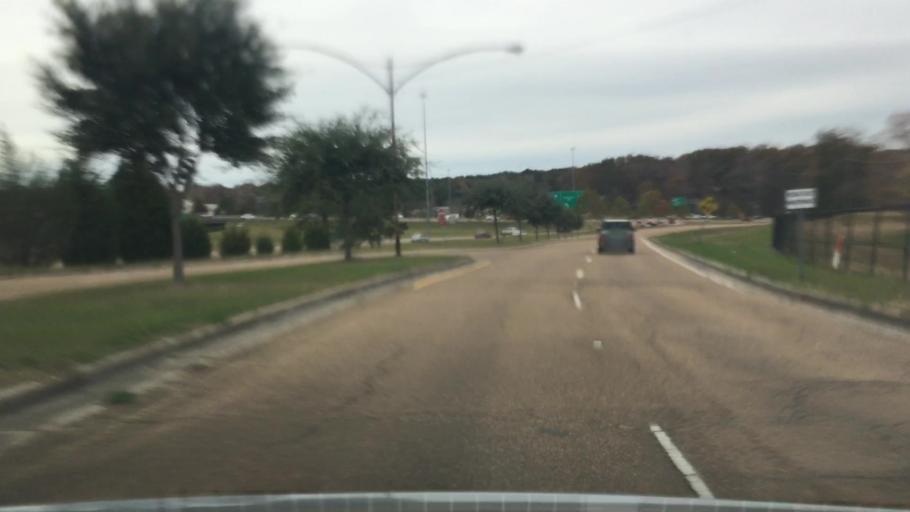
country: US
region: Mississippi
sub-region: Rankin County
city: Flowood
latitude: 32.3307
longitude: -90.1612
